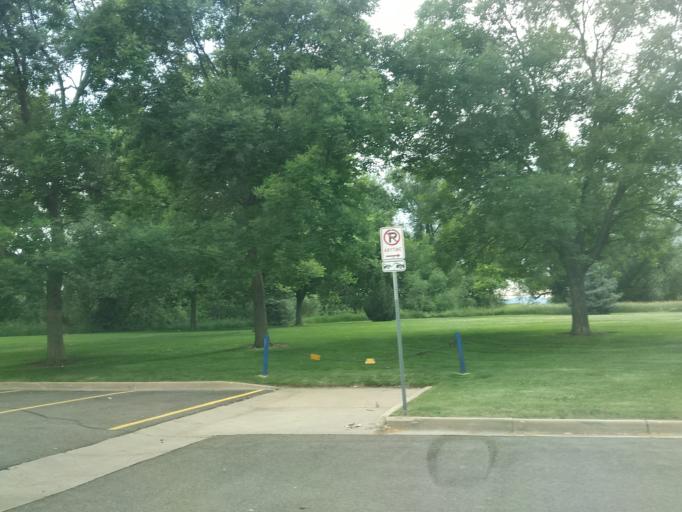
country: US
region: Colorado
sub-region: Jefferson County
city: Lakewood
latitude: 39.7043
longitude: -105.1029
